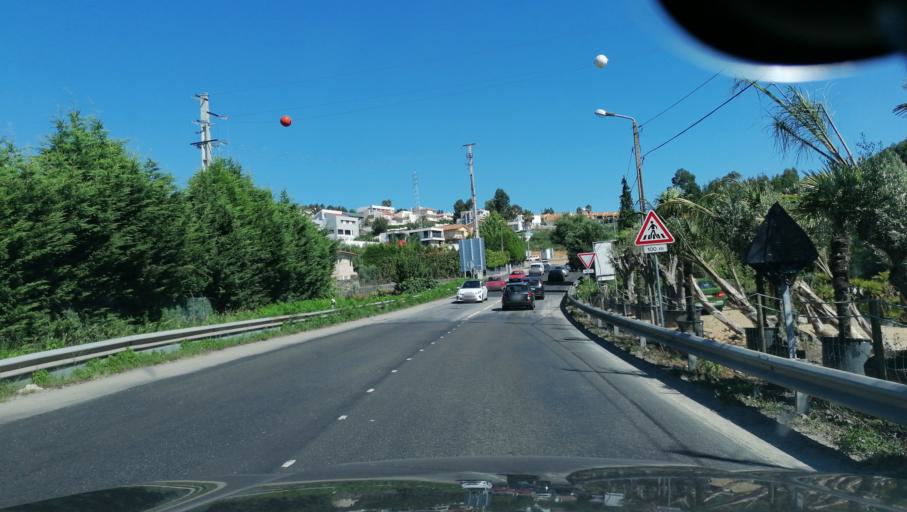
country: PT
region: Aveiro
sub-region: Santa Maria da Feira
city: Arrifana
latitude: 40.9300
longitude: -8.5131
